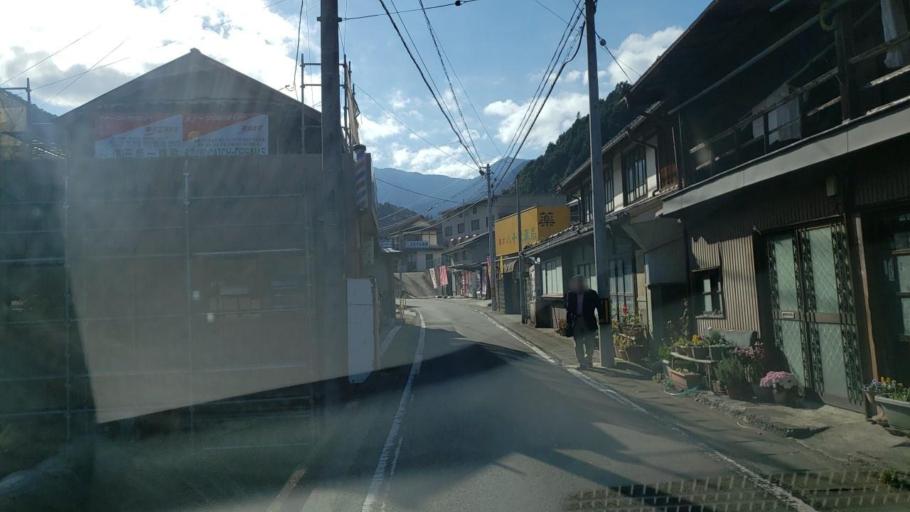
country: JP
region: Tokushima
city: Wakimachi
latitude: 33.9980
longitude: 134.0281
